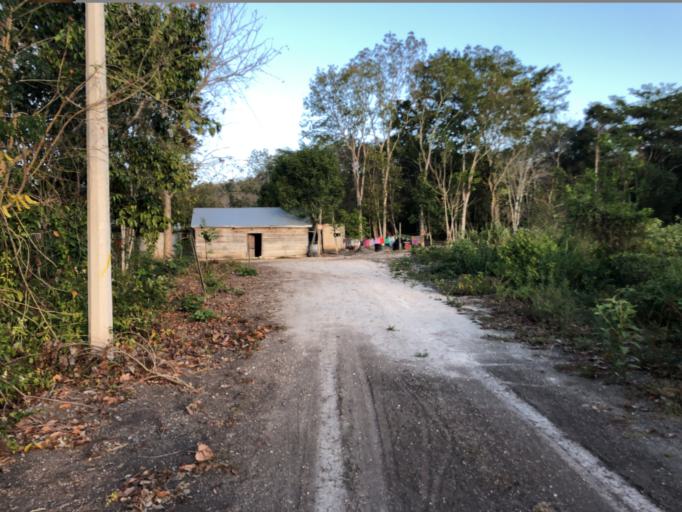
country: MX
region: Quintana Roo
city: Nicolas Bravo
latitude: 18.4495
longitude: -89.3054
